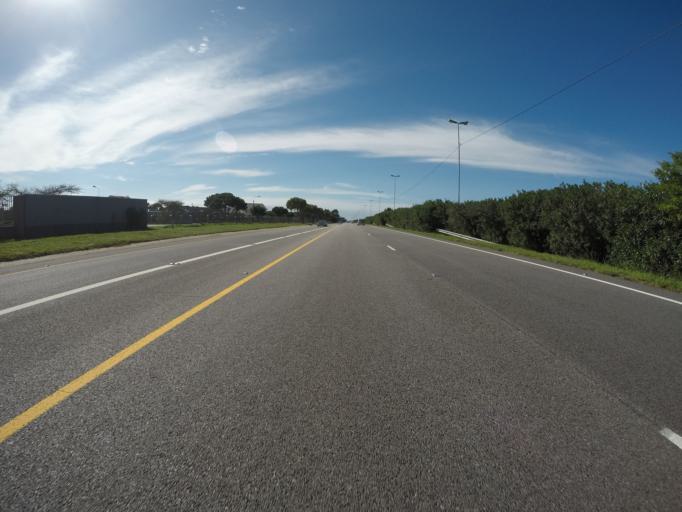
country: ZA
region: Eastern Cape
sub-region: Nelson Mandela Bay Metropolitan Municipality
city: Port Elizabeth
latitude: -33.9479
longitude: 25.5162
